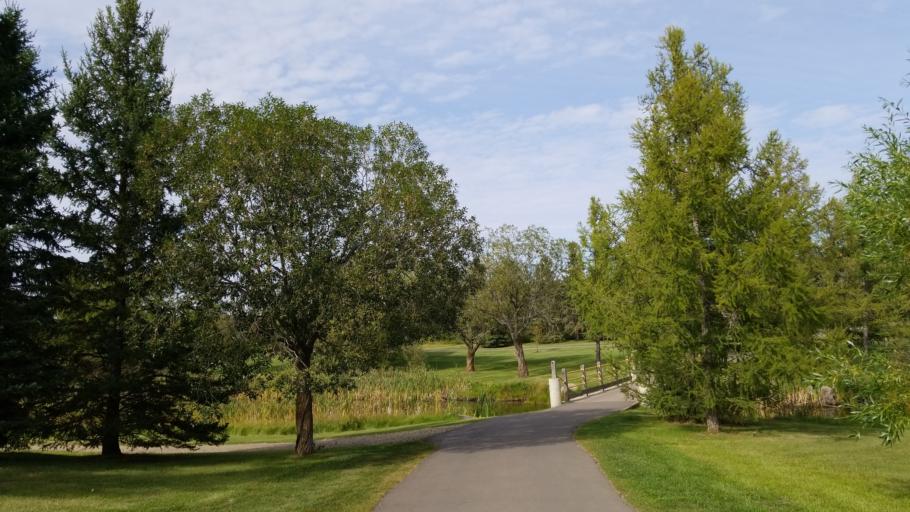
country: CA
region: Saskatchewan
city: Lloydminster
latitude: 53.2594
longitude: -110.0422
